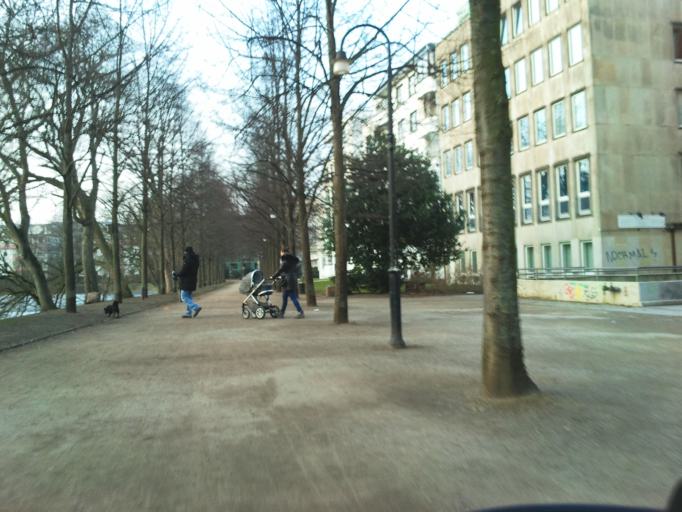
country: DE
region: Bremen
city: Bremen
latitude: 53.0799
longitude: 8.8088
